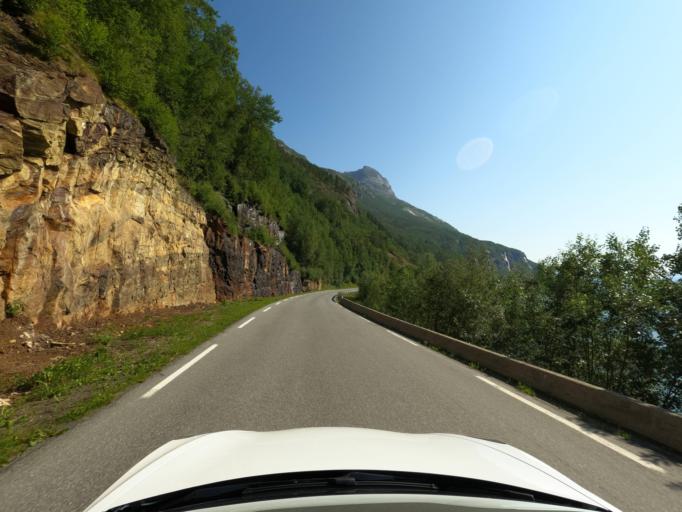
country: NO
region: Nordland
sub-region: Narvik
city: Narvik
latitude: 68.3592
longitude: 17.2664
